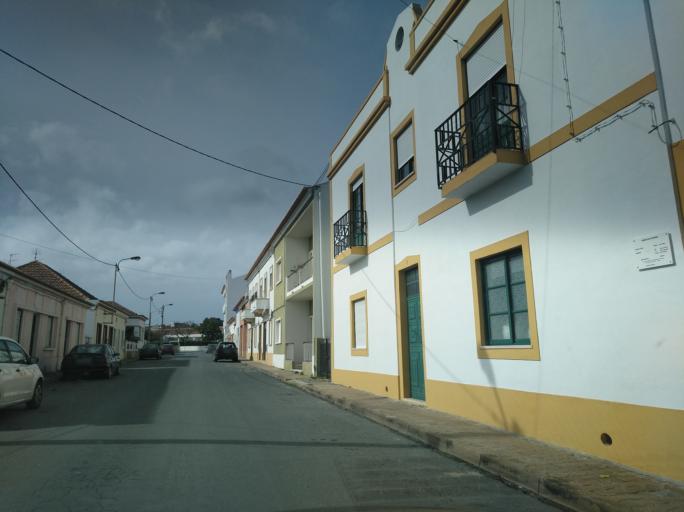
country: PT
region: Setubal
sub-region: Grandola
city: Grandola
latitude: 38.1772
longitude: -8.5609
